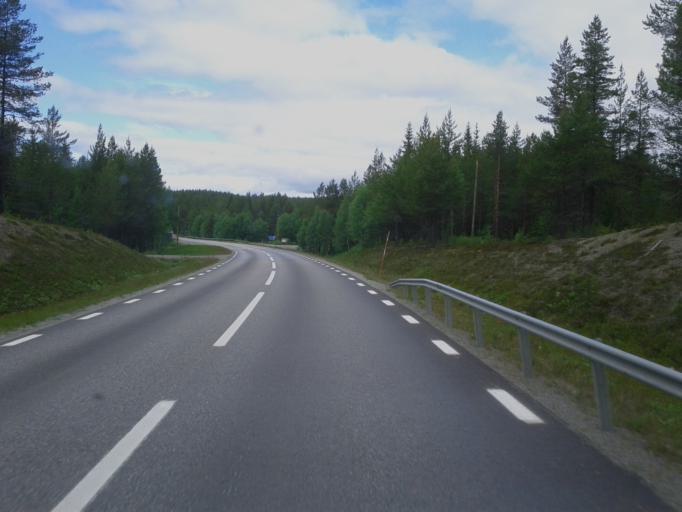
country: SE
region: Vaesterbotten
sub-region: Storumans Kommun
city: Fristad
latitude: 65.3817
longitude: 16.5106
